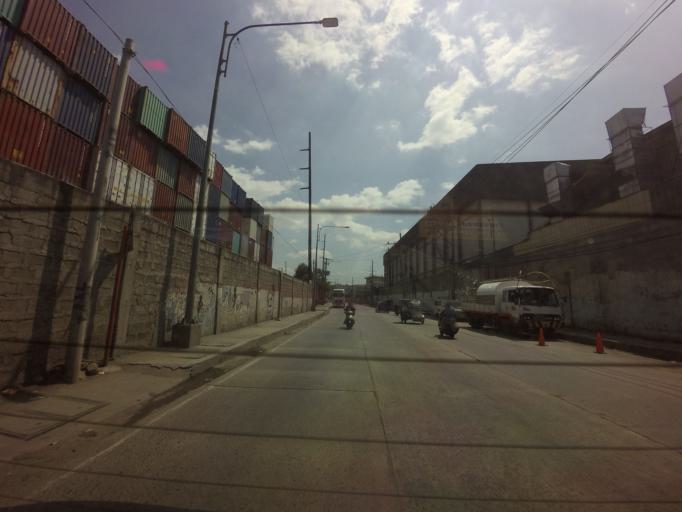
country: PH
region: Metro Manila
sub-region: Caloocan City
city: Niugan
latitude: 14.6398
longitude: 120.9574
